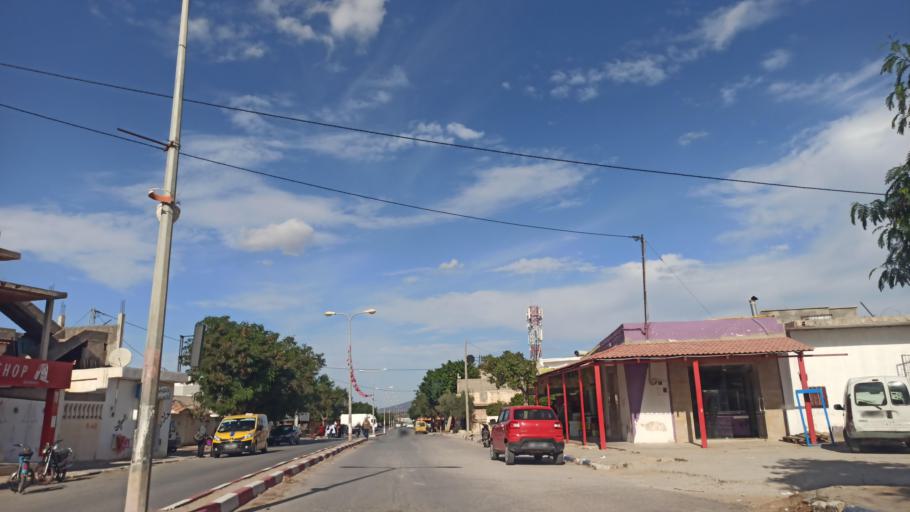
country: TN
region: Zaghwan
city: Zaghouan
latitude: 36.3531
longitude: 10.2095
